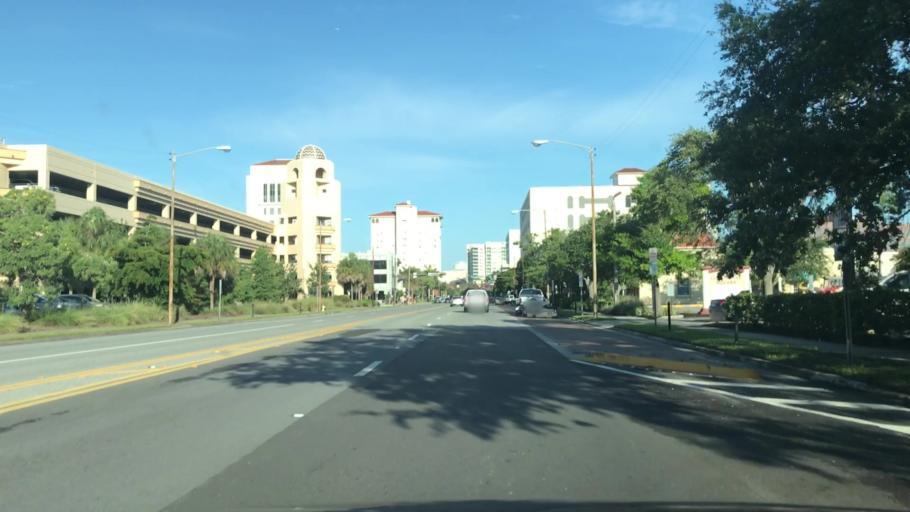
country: US
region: Florida
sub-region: Sarasota County
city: Sarasota
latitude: 27.3357
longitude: -82.5265
